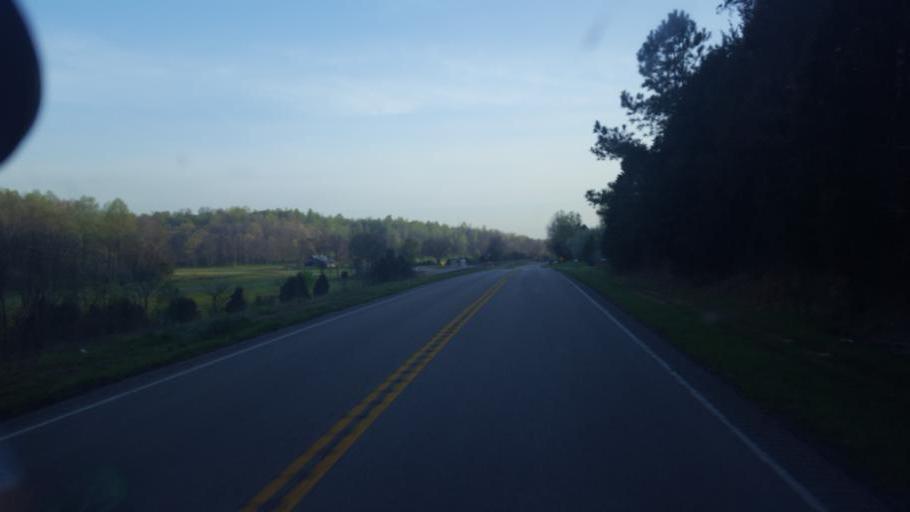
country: US
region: Kentucky
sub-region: Hart County
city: Munfordville
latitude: 37.3457
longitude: -85.9098
